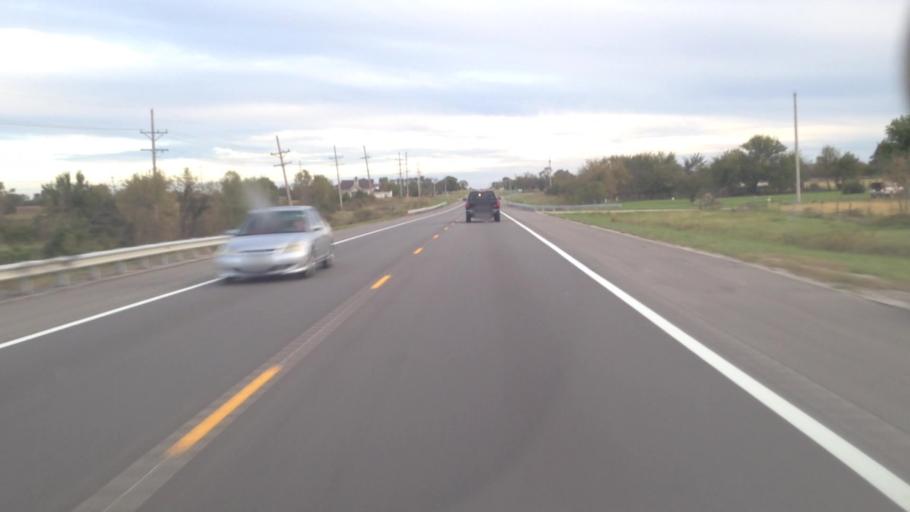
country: US
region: Kansas
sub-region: Franklin County
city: Ottawa
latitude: 38.5538
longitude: -95.2678
